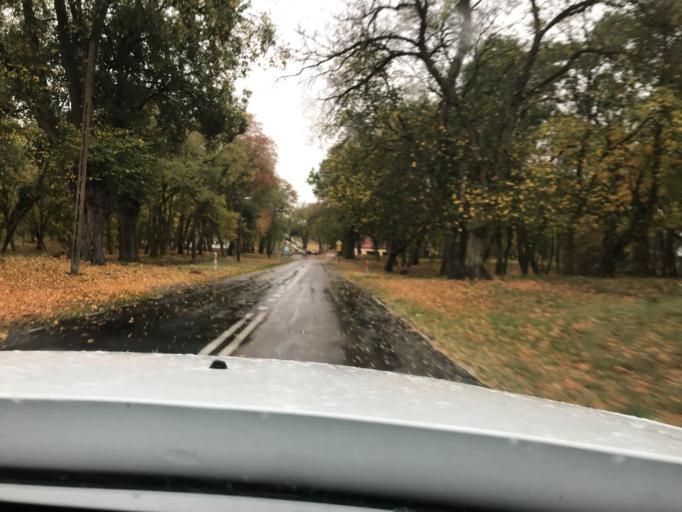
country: DE
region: Brandenburg
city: Neulewin
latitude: 52.7663
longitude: 14.3222
